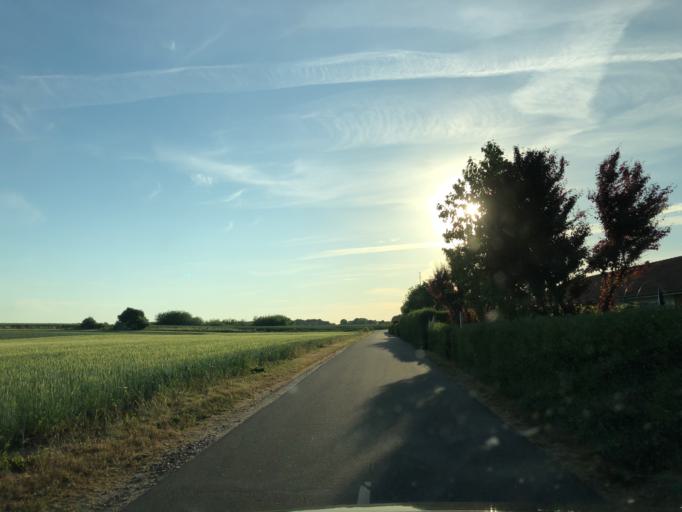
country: DK
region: Central Jutland
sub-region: Struer Kommune
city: Struer
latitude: 56.4776
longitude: 8.5724
